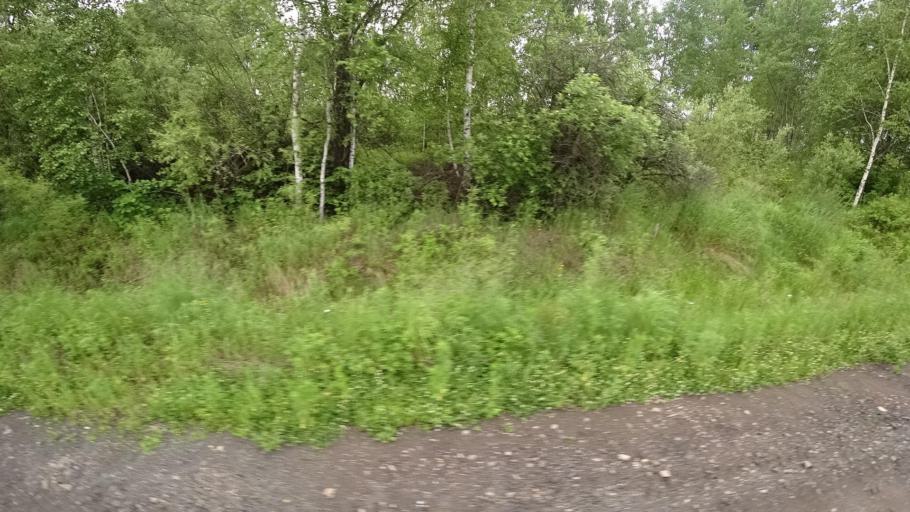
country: RU
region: Khabarovsk Krai
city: Amursk
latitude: 49.9104
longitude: 136.1562
